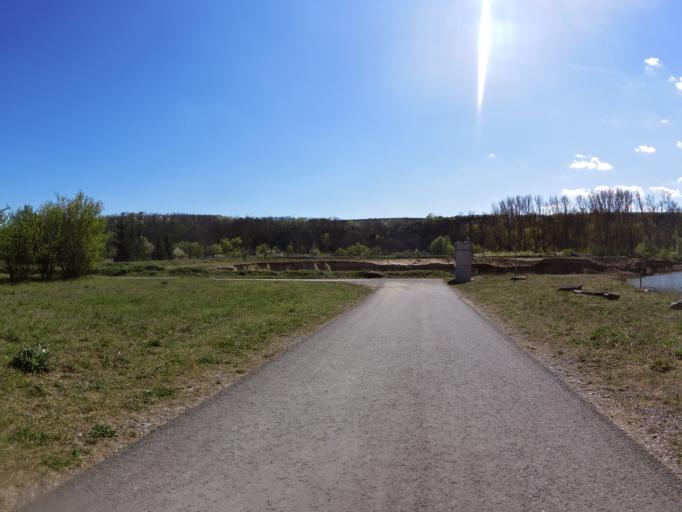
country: DE
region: Bavaria
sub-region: Regierungsbezirk Unterfranken
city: Nordheim
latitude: 49.8582
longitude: 10.2068
